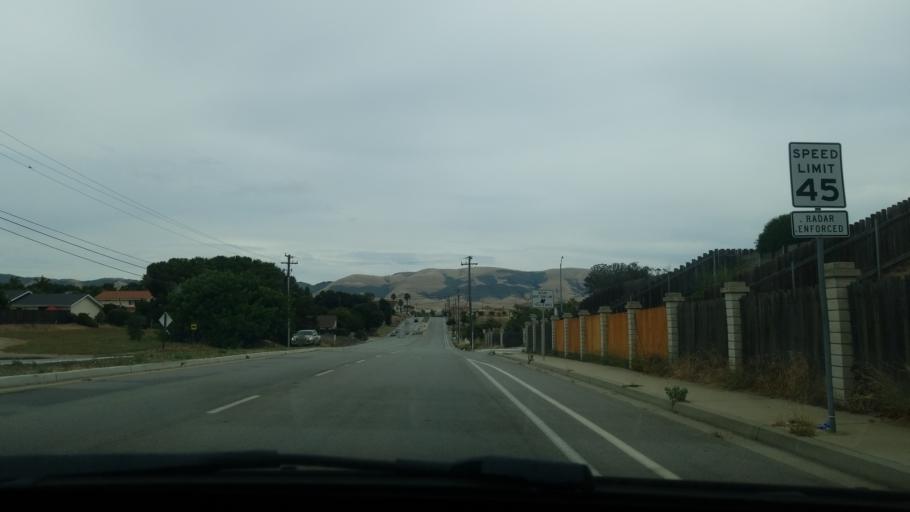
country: US
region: California
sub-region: San Luis Obispo County
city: Nipomo
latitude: 35.0314
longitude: -120.4942
